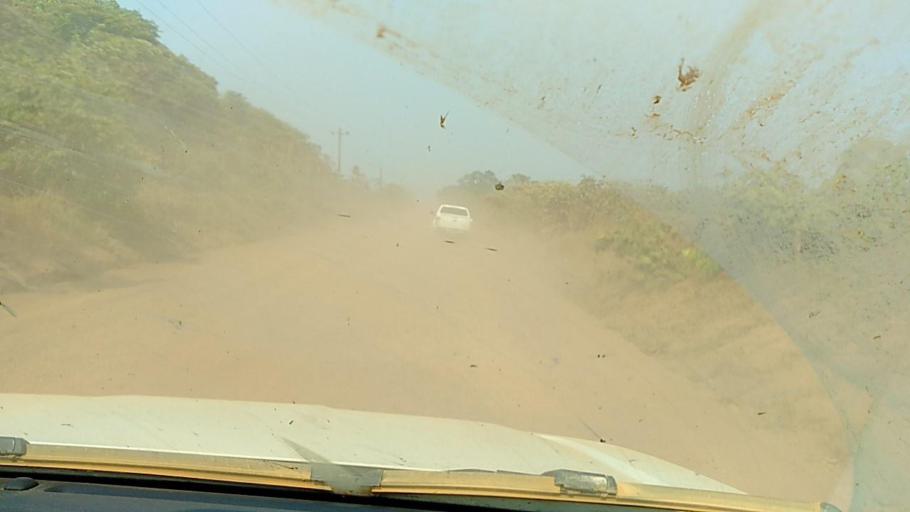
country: BR
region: Rondonia
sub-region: Porto Velho
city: Porto Velho
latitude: -8.8387
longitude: -64.1508
